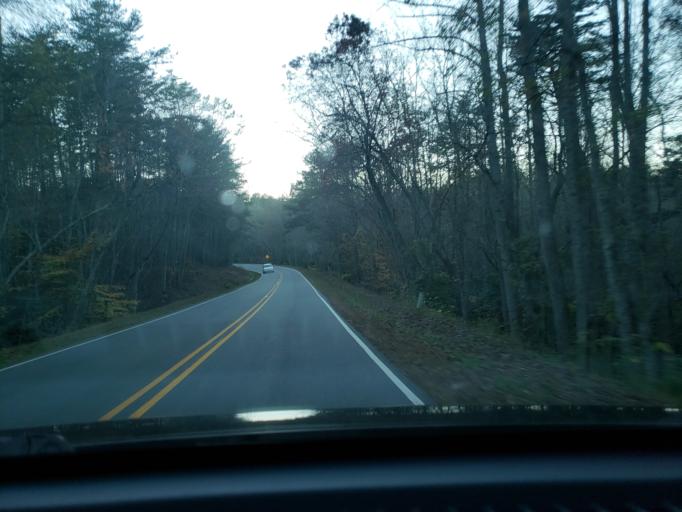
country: US
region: North Carolina
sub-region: Stokes County
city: Danbury
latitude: 36.4131
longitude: -80.2515
